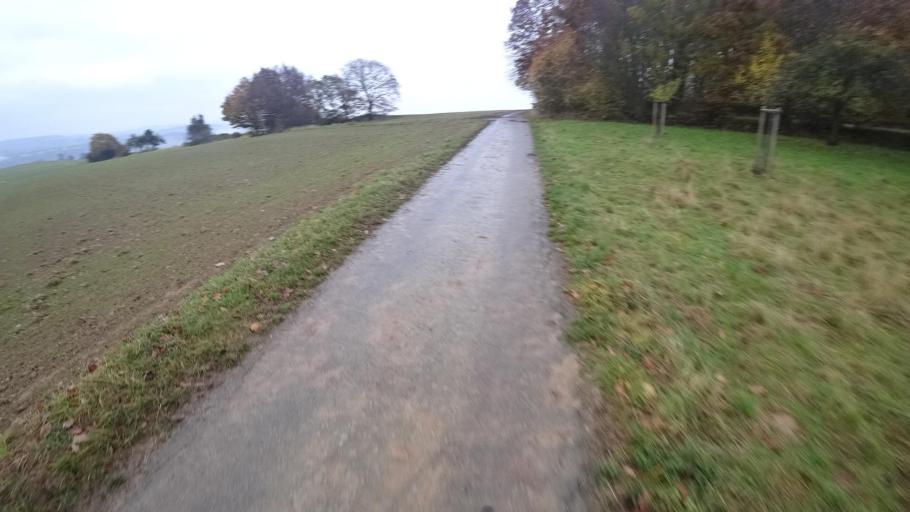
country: DE
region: Rheinland-Pfalz
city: Sankt Goar
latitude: 50.1379
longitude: 7.6955
